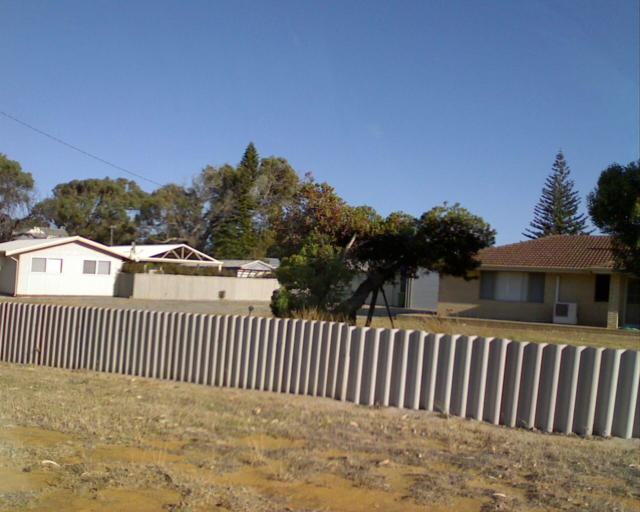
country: AU
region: Western Australia
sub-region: Dandaragan
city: Jurien Bay
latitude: -30.0658
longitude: 114.9679
